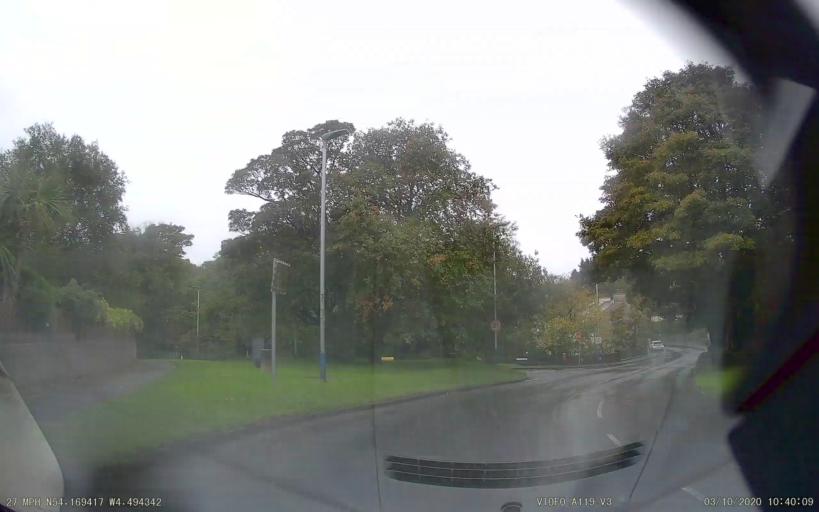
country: IM
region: Douglas
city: Douglas
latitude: 54.1694
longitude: -4.4943
